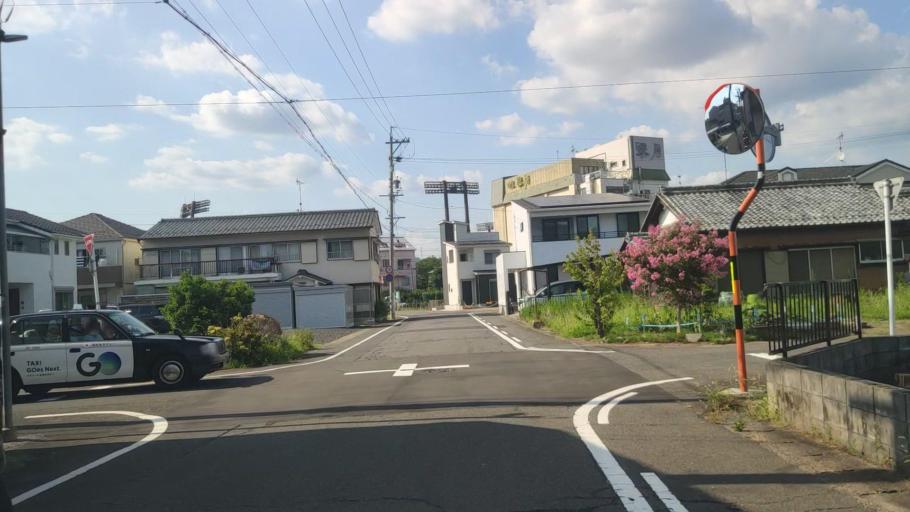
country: JP
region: Gifu
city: Gifu-shi
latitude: 35.4376
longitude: 136.7639
